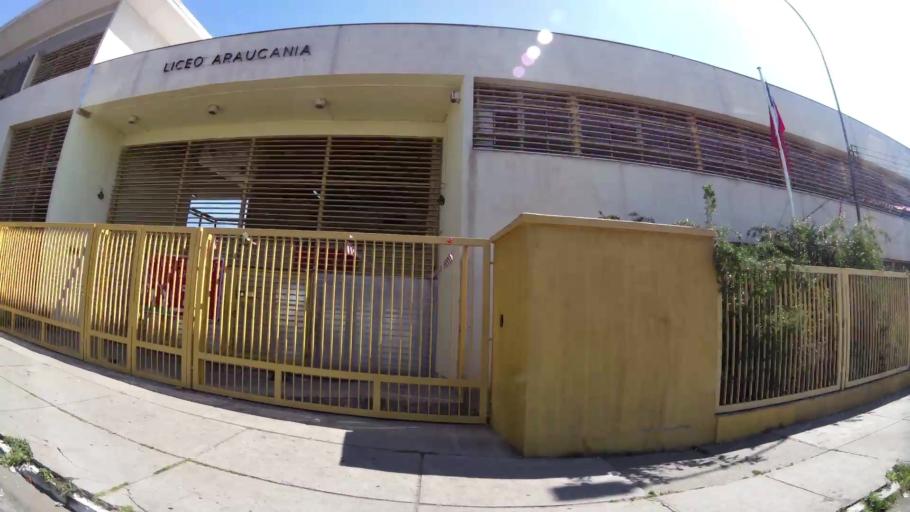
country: CL
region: Santiago Metropolitan
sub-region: Provincia de Santiago
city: La Pintana
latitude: -33.5347
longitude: -70.6372
